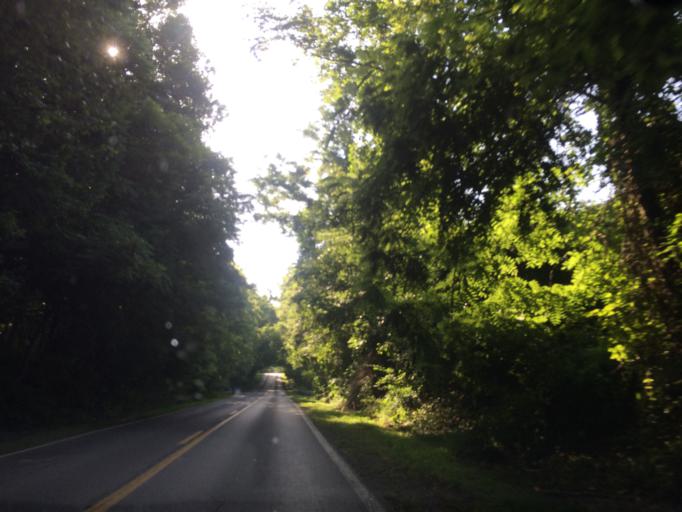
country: US
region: Maryland
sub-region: Montgomery County
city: Ashton-Sandy Spring
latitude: 39.1921
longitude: -77.0217
